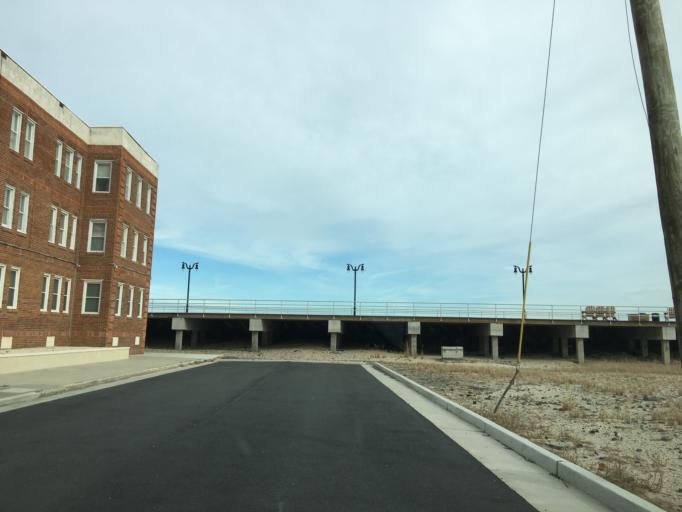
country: US
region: New Jersey
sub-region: Atlantic County
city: Atlantic City
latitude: 39.3679
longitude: -74.4115
